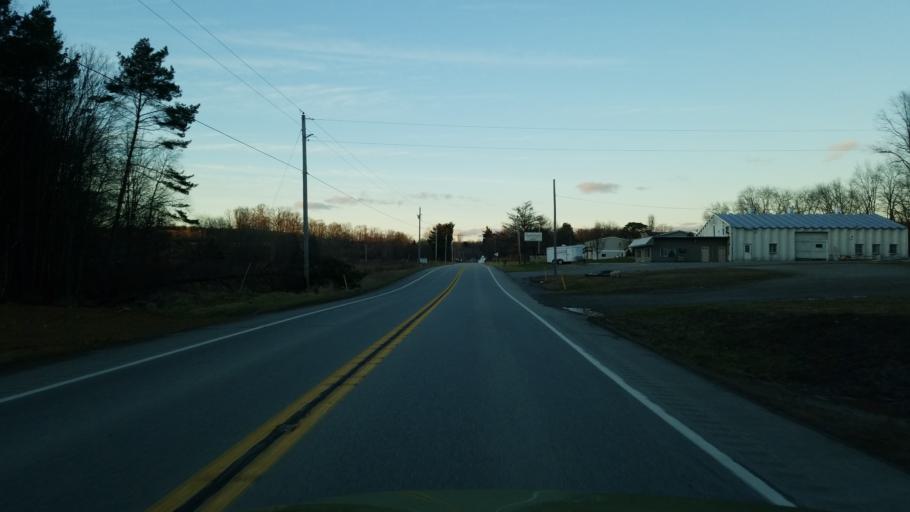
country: US
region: Pennsylvania
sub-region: Indiana County
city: Clymer
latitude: 40.7845
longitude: -79.0535
